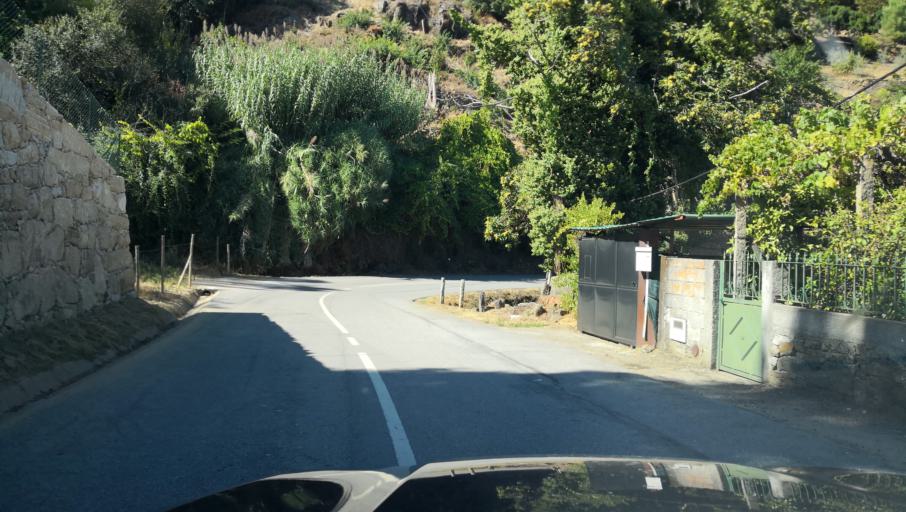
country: PT
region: Vila Real
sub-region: Santa Marta de Penaguiao
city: Santa Marta de Penaguiao
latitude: 41.2314
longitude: -7.7939
